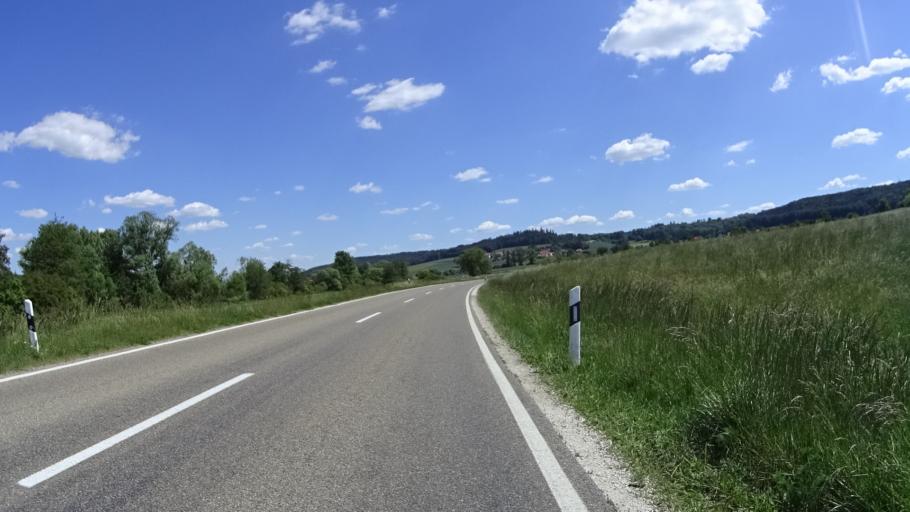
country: DE
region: Bavaria
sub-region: Regierungsbezirk Mittelfranken
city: Thalmassing
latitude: 49.0858
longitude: 11.2384
